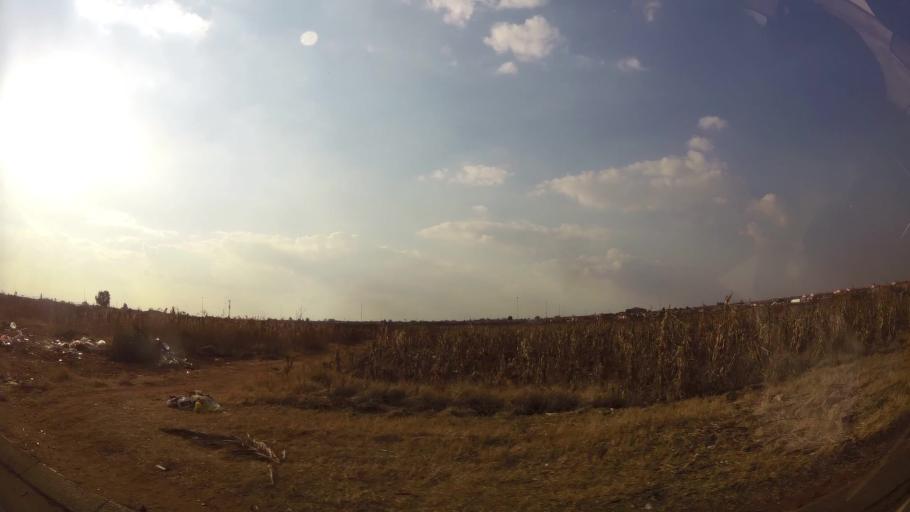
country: ZA
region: Gauteng
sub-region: Ekurhuleni Metropolitan Municipality
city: Germiston
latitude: -26.3697
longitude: 28.1947
